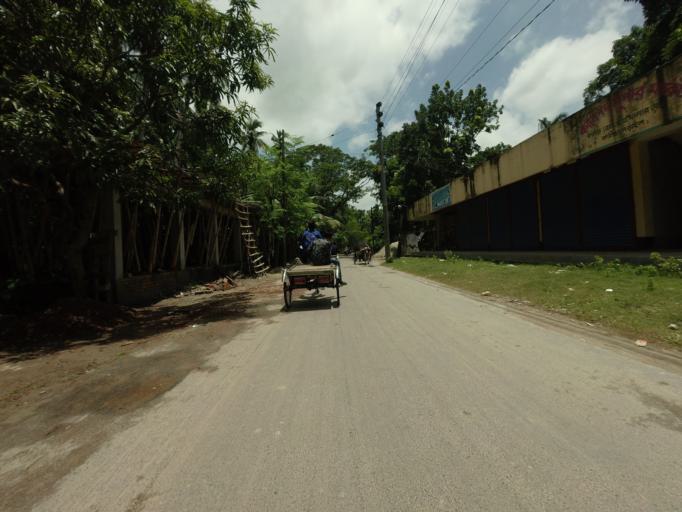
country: BD
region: Khulna
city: Kalia
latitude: 23.0359
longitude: 89.6328
